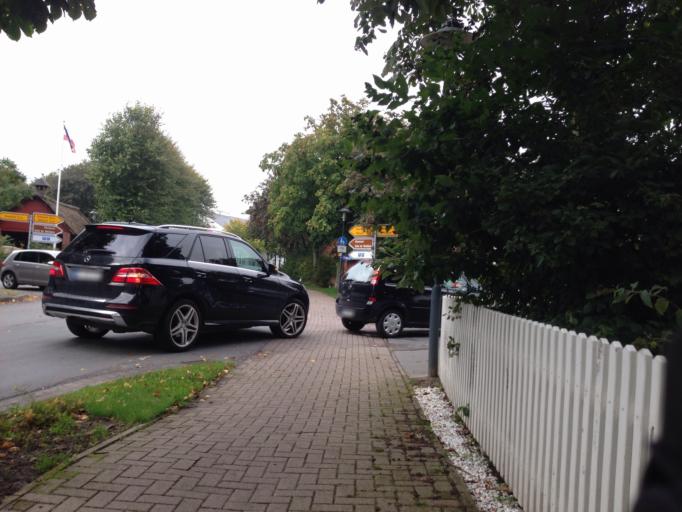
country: DE
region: Schleswig-Holstein
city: Alkersum
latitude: 54.7082
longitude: 8.5116
